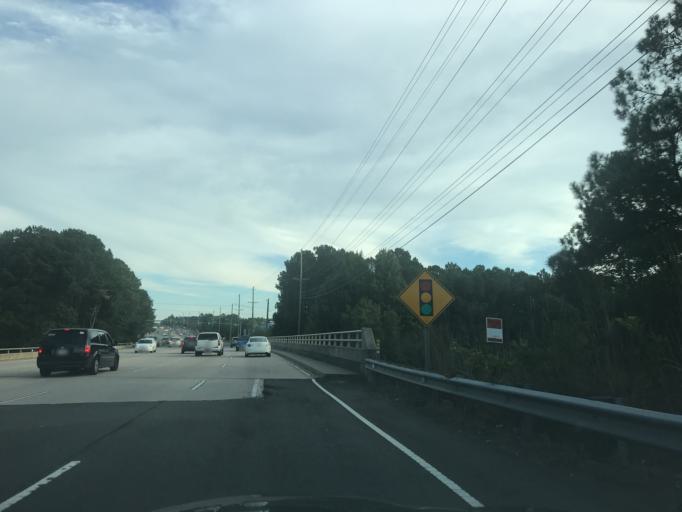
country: US
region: North Carolina
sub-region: Wake County
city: Apex
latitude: 35.7489
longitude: -78.8760
